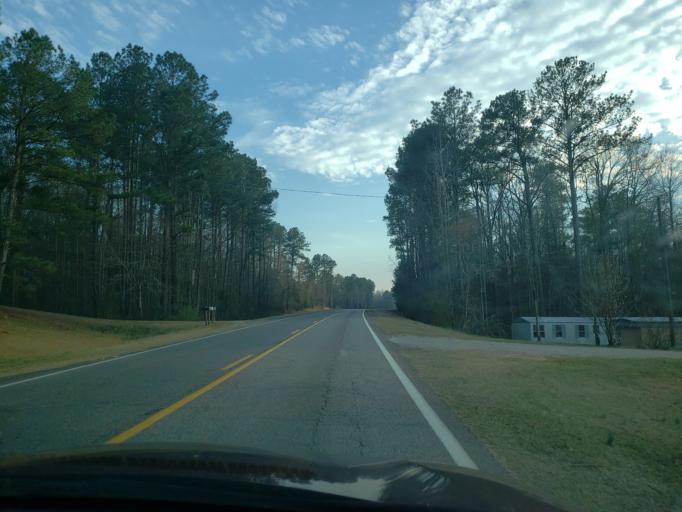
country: US
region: Alabama
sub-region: Hale County
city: Greensboro
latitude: 32.7344
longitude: -87.5863
